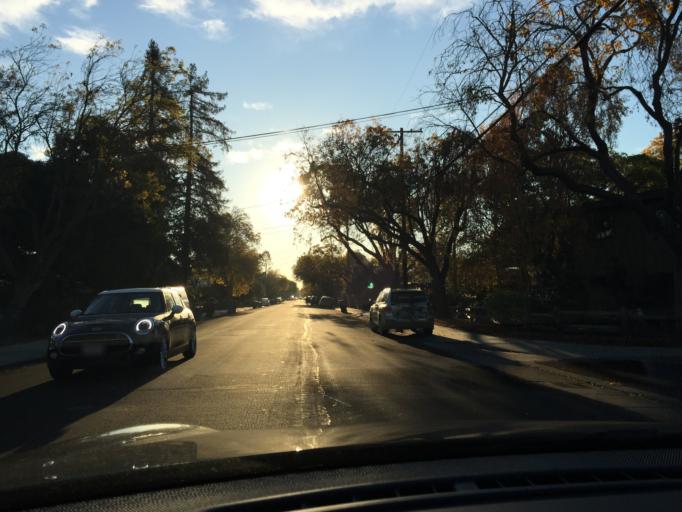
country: US
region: California
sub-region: Santa Clara County
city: Palo Alto
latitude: 37.4329
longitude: -122.1223
